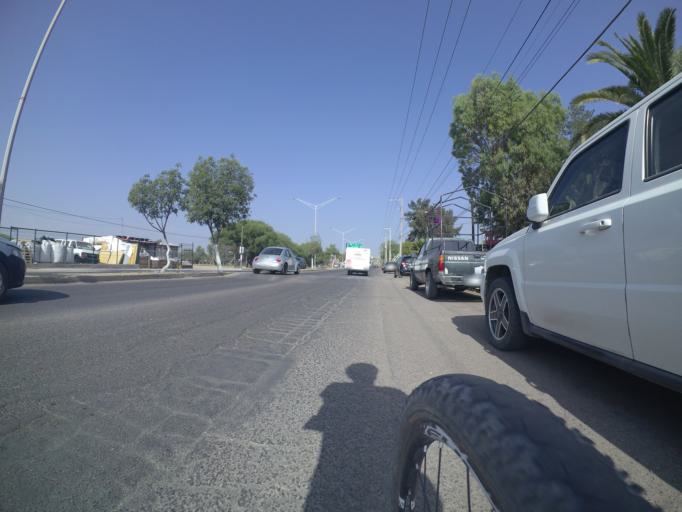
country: MX
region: Aguascalientes
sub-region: Jesus Maria
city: Corral de Barrancos
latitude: 21.9519
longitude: -102.3303
